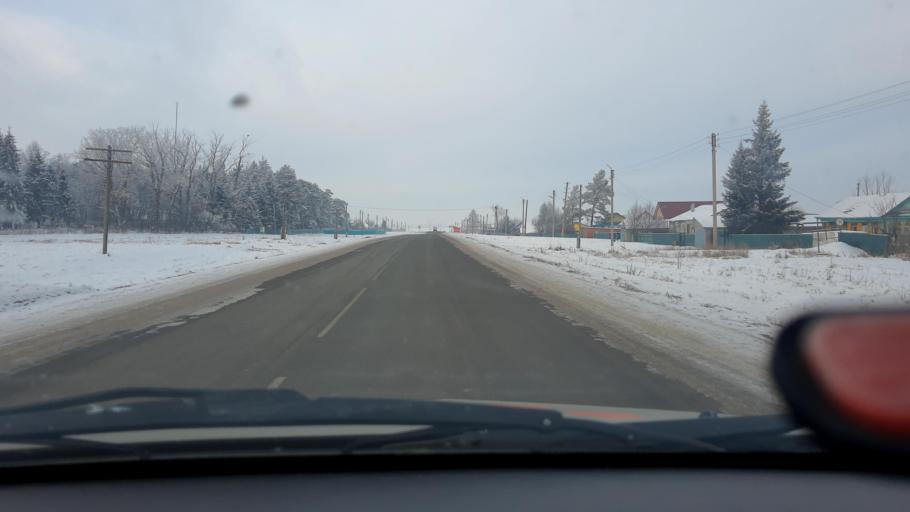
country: RU
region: Bashkortostan
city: Avdon
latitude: 54.3771
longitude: 55.8103
